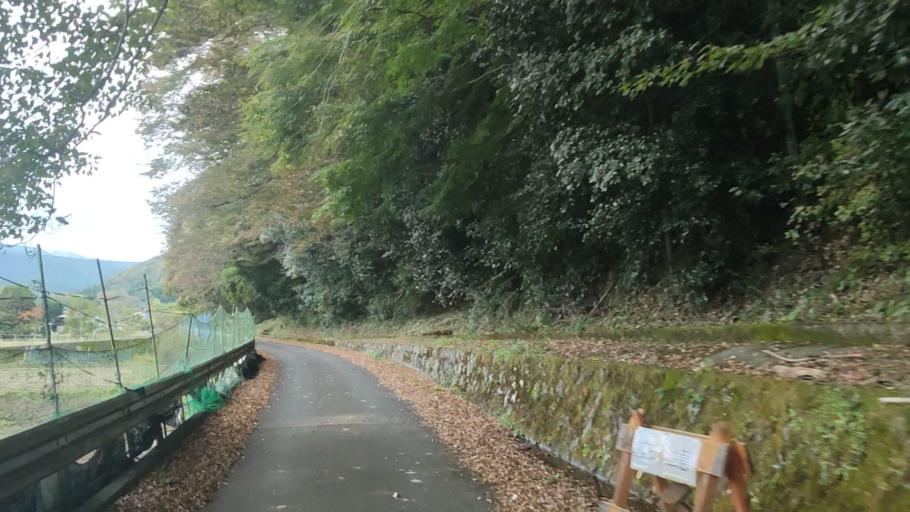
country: JP
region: Shizuoka
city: Ito
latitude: 34.9343
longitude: 138.9926
